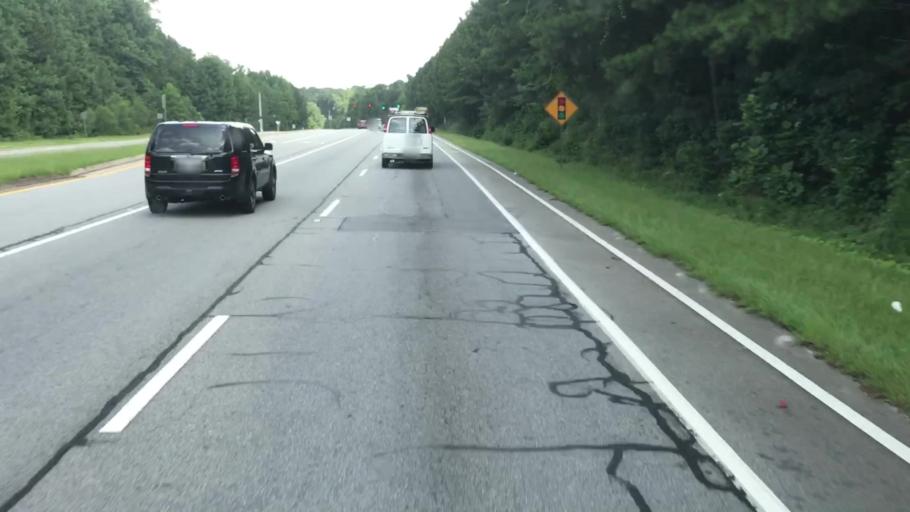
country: US
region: Georgia
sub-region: Gwinnett County
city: Suwanee
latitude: 33.9776
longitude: -84.0742
